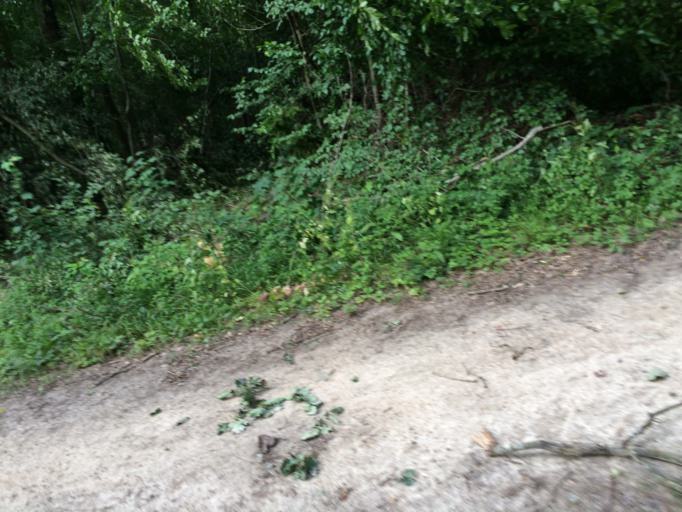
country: FR
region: Ile-de-France
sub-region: Departement de l'Essonne
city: Ris-Orangis
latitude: 48.6652
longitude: 2.4328
